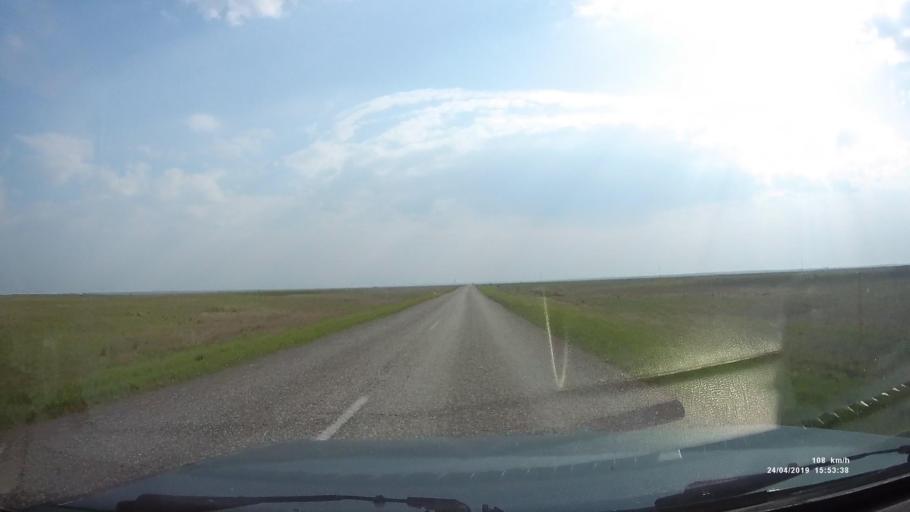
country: RU
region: Kalmykiya
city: Yashalta
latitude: 46.5956
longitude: 42.5730
